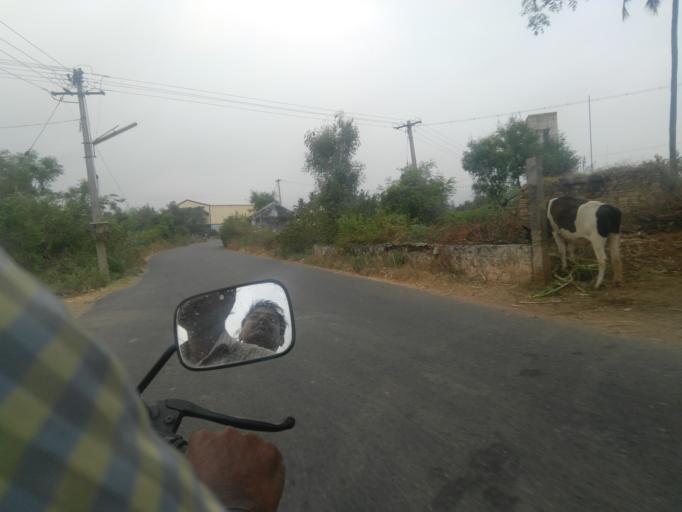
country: IN
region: Tamil Nadu
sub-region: Coimbatore
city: Karamadai
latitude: 11.2611
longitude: 76.9446
